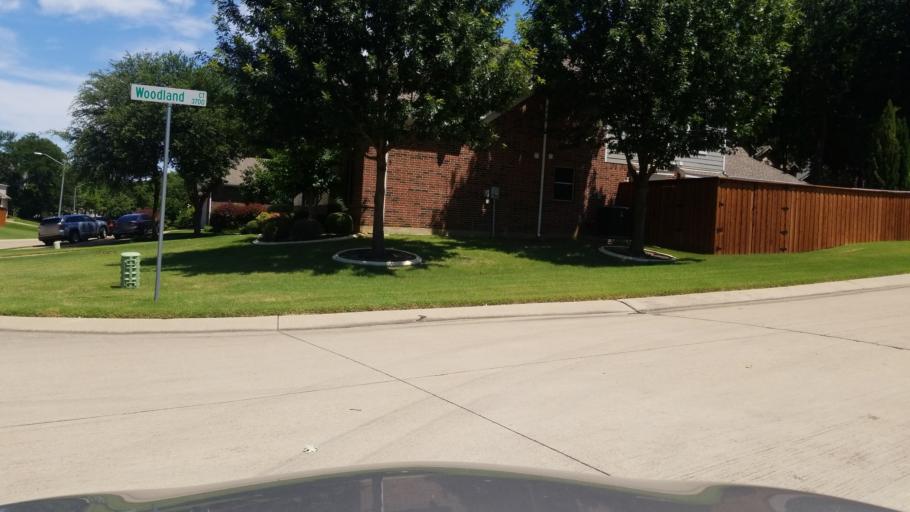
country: US
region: Texas
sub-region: Dallas County
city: Grand Prairie
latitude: 32.6834
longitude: -97.0019
